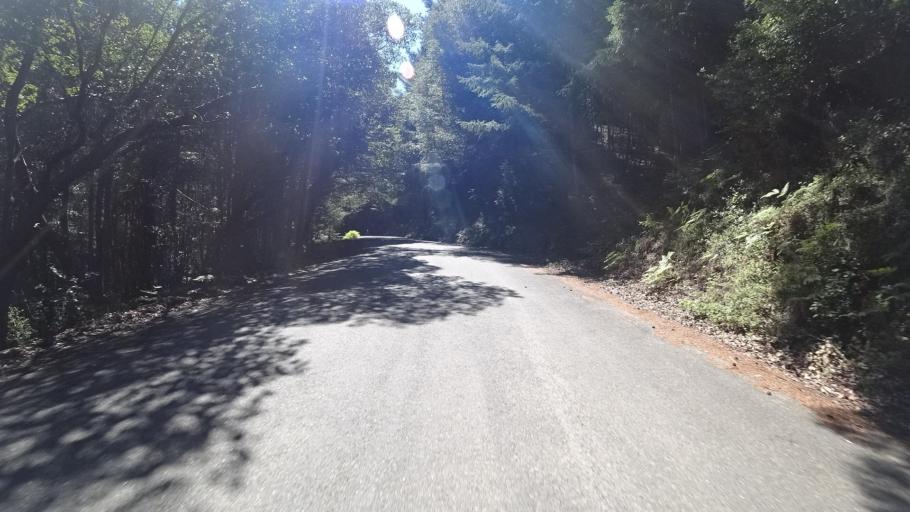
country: US
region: California
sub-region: Humboldt County
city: Redway
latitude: 40.1308
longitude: -123.9784
